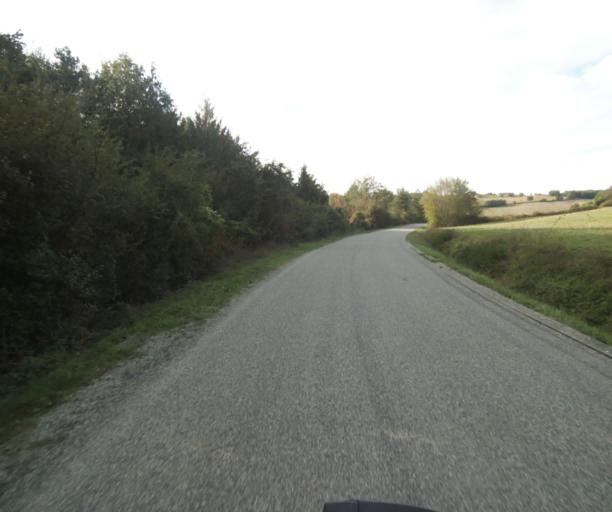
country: FR
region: Midi-Pyrenees
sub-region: Departement du Tarn-et-Garonne
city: Finhan
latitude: 43.9135
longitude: 1.1090
